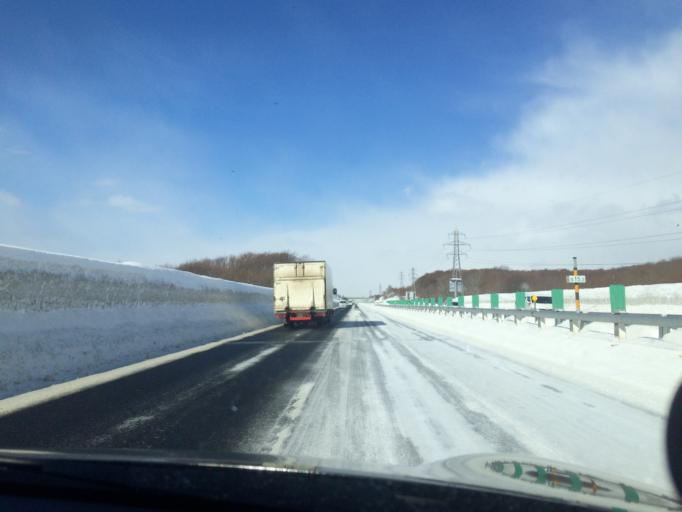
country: JP
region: Hokkaido
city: Kitahiroshima
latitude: 42.9580
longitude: 141.5039
